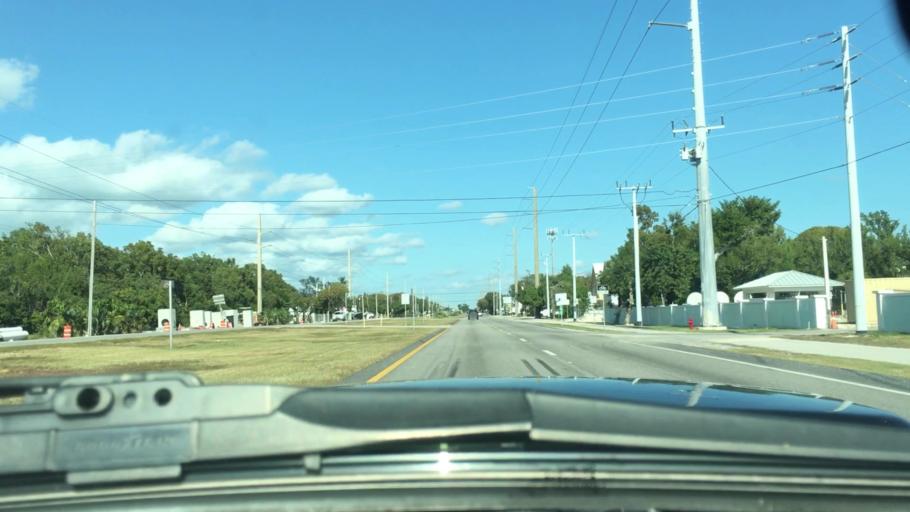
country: US
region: Florida
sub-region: Monroe County
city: Tavernier
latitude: 25.0451
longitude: -80.4903
